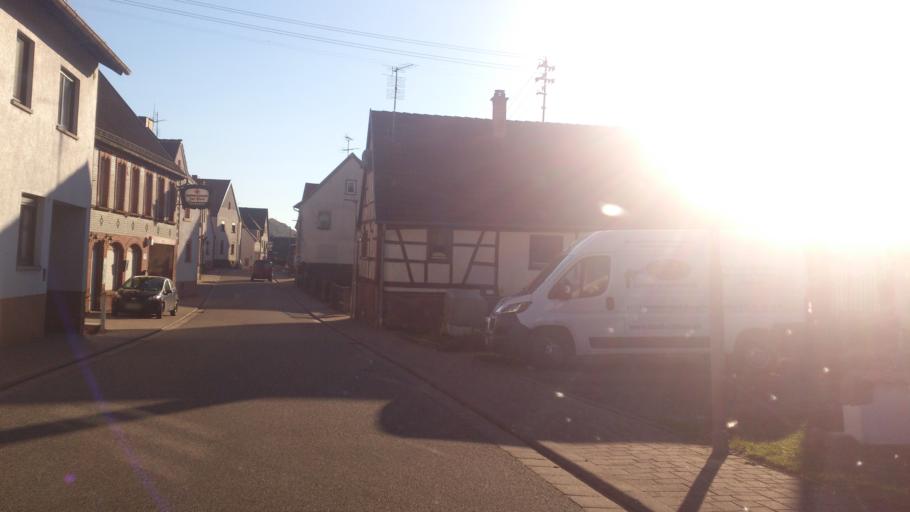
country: DE
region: Rheinland-Pfalz
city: Leimen
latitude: 49.2758
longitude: 7.7740
